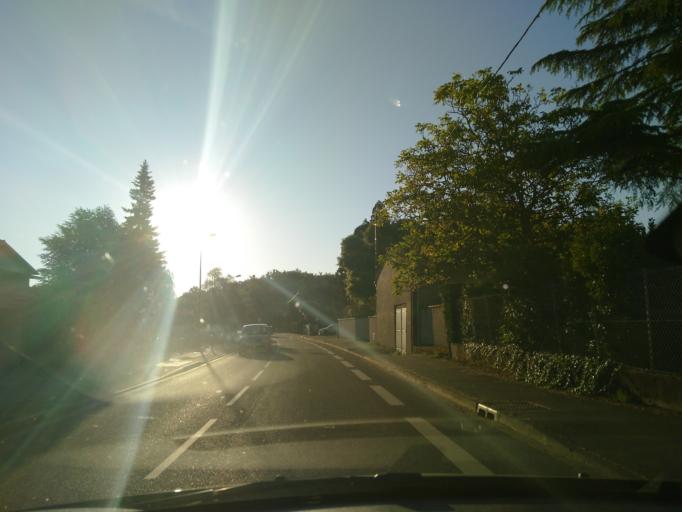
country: FR
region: Midi-Pyrenees
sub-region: Departement de la Haute-Garonne
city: Aussonne
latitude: 43.6840
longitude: 1.3238
